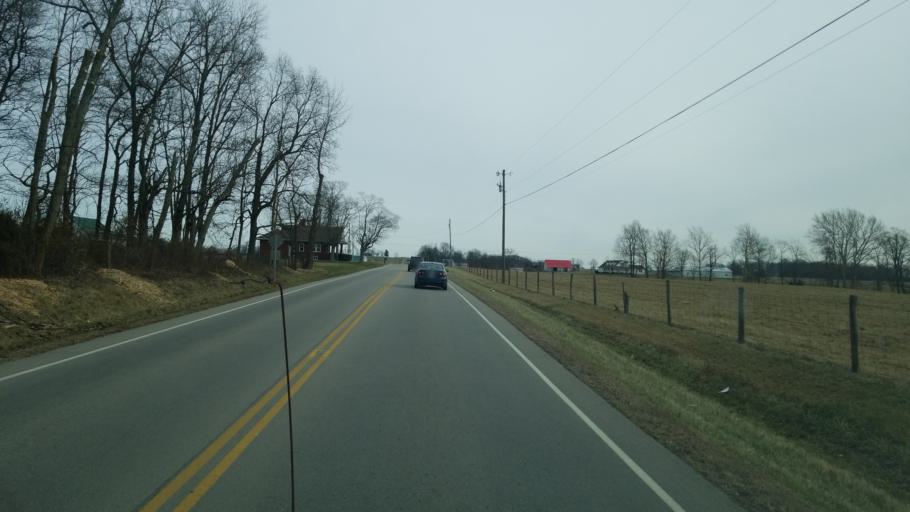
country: US
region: Ohio
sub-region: Adams County
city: Winchester
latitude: 39.0652
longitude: -83.6975
